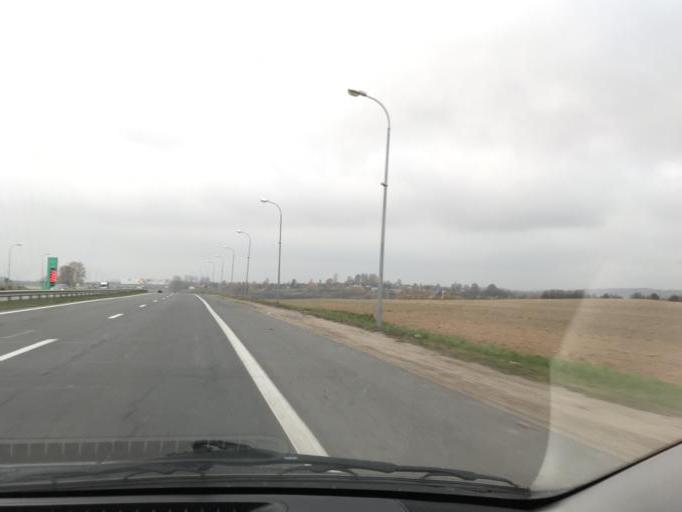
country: BY
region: Vitebsk
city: Vitebsk
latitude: 55.1529
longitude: 30.1293
